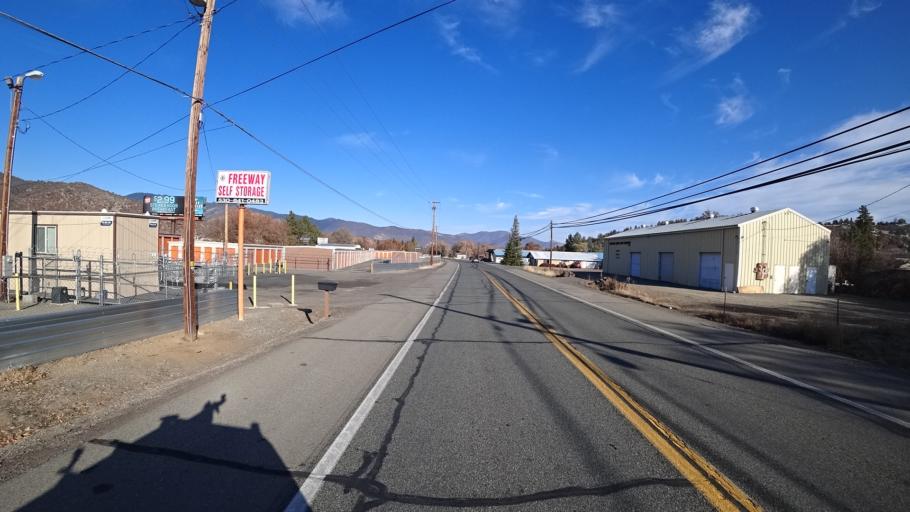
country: US
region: California
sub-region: Siskiyou County
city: Yreka
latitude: 41.6972
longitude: -122.6392
